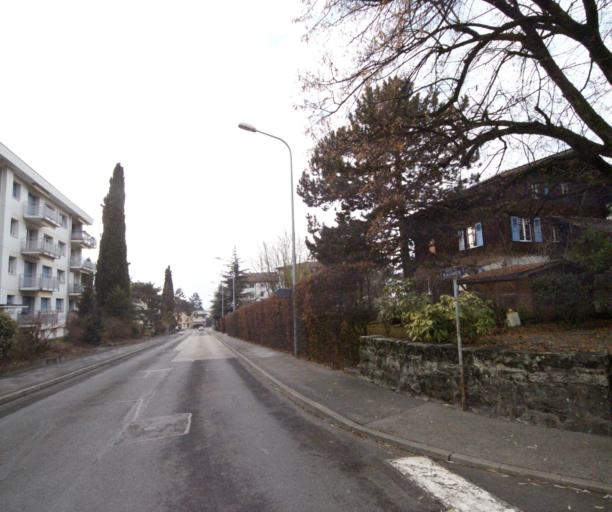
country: CH
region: Vaud
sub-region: Riviera-Pays-d'Enhaut District
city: La Tour-de-Peilz
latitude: 46.4561
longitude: 6.8637
